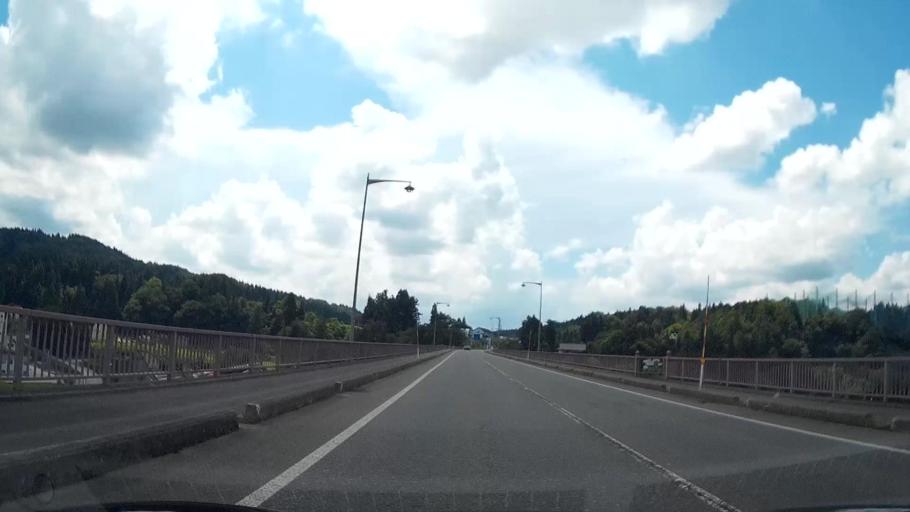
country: JP
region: Niigata
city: Tokamachi
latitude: 37.0452
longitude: 138.6870
